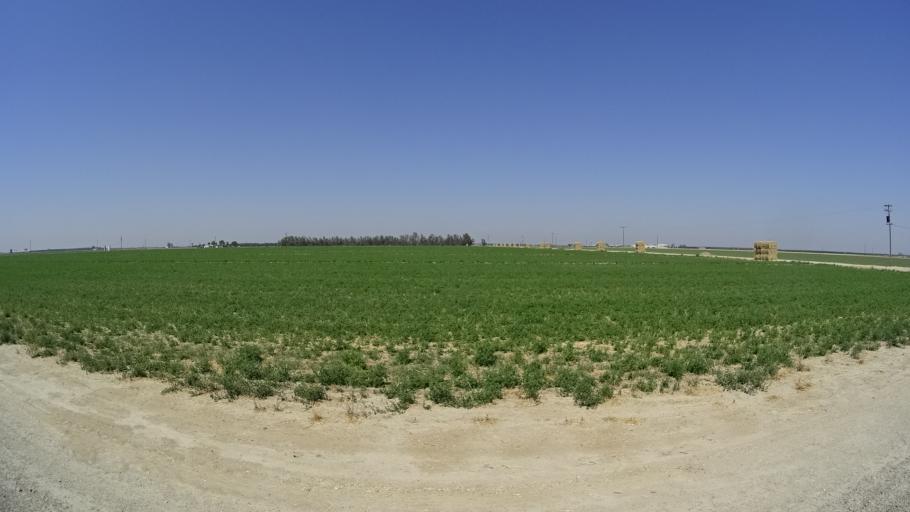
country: US
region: California
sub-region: Tulare County
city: Goshen
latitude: 36.3753
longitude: -119.5290
